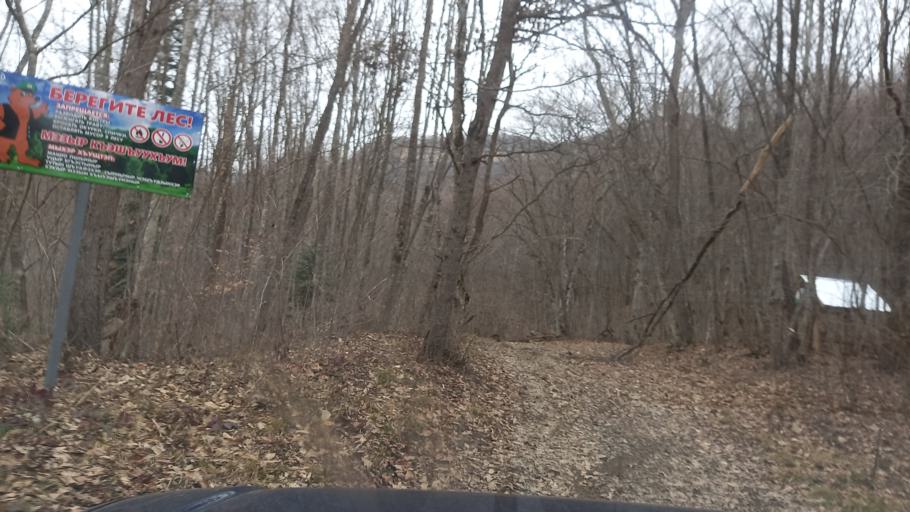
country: RU
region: Adygeya
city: Kamennomostskiy
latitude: 44.1111
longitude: 40.1038
